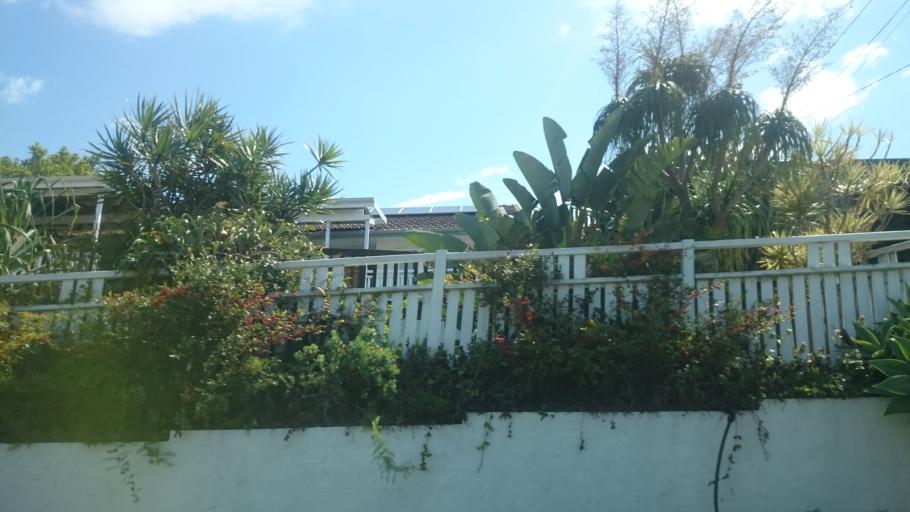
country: AU
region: Queensland
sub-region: Brisbane
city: Manly West
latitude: -27.4648
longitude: 153.1745
